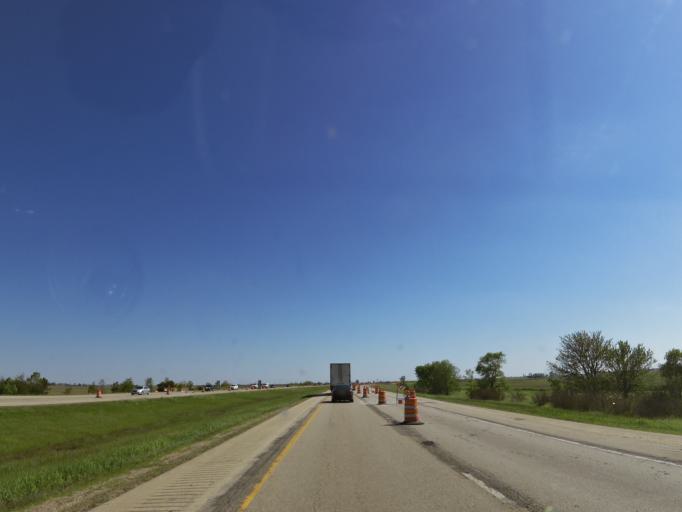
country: US
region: Illinois
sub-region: Ogle County
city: Hillcrest
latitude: 41.9750
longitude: -89.0210
